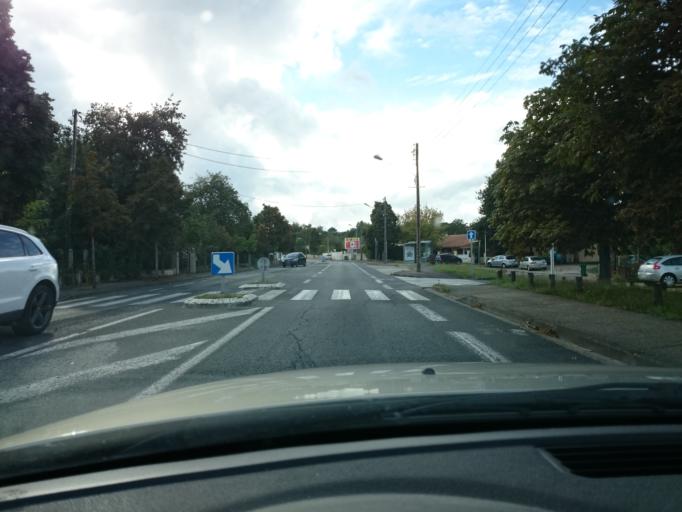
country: FR
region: Aquitaine
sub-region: Departement de la Gironde
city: Pessac
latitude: 44.8018
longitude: -0.6807
